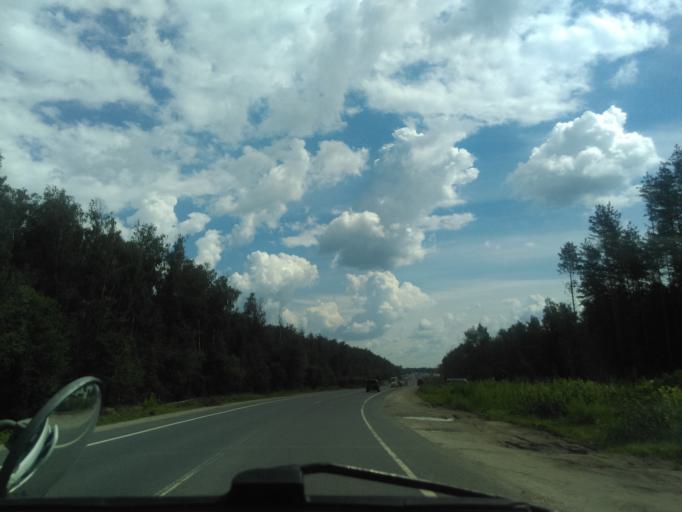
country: RU
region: Moskovskaya
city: Vostryakovo
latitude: 55.4273
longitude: 37.8519
